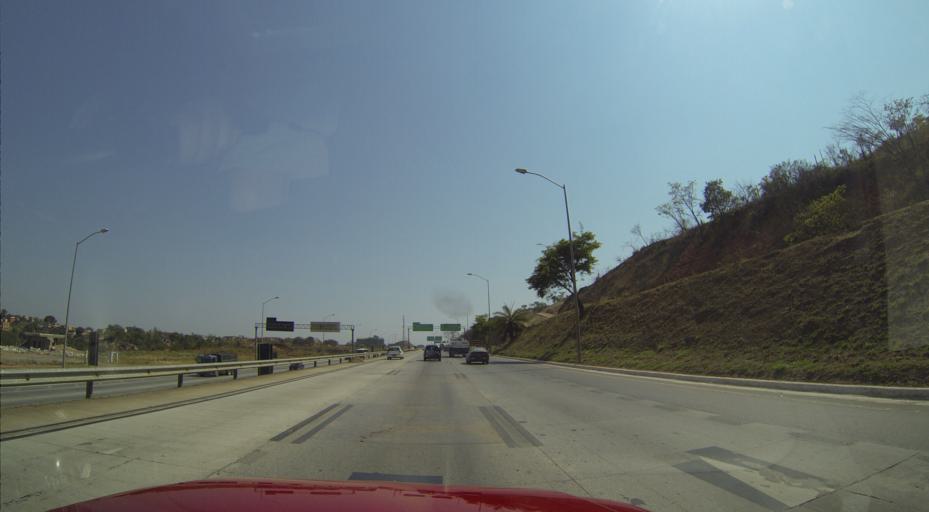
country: BR
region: Minas Gerais
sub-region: Vespasiano
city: Vespasiano
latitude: -19.7658
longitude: -43.9482
